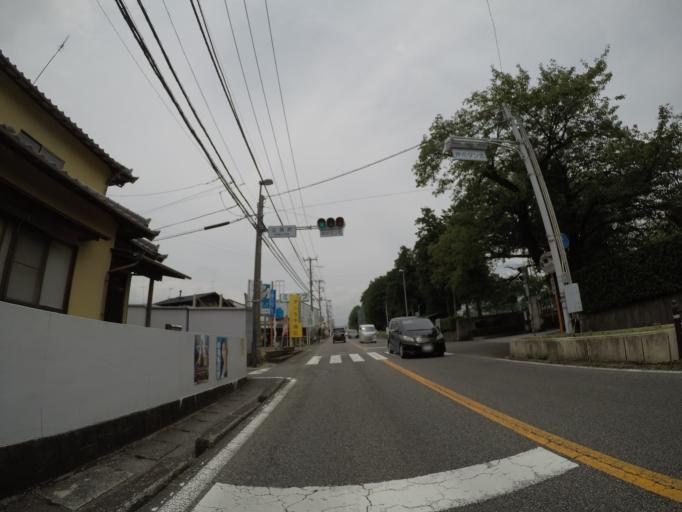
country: JP
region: Shizuoka
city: Fujinomiya
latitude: 35.2371
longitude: 138.6095
